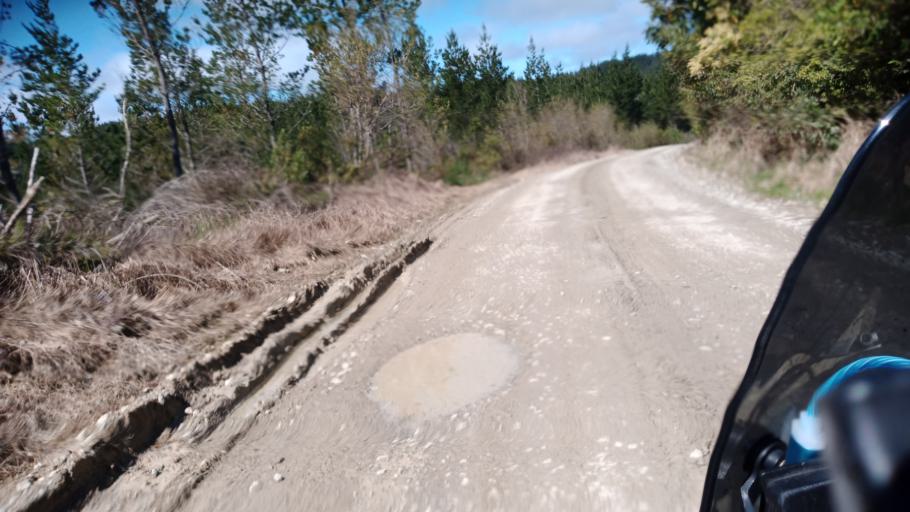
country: NZ
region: Gisborne
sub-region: Gisborne District
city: Gisborne
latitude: -38.9095
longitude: 177.8146
